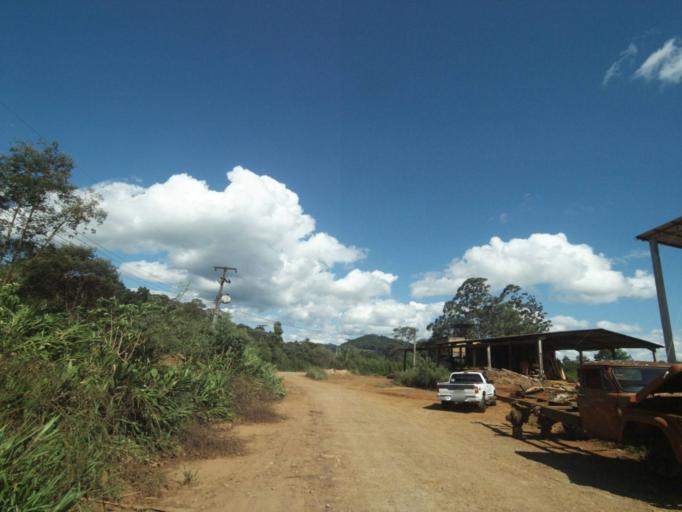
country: BR
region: Parana
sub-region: Uniao Da Vitoria
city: Uniao da Vitoria
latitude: -26.1499
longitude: -51.5394
